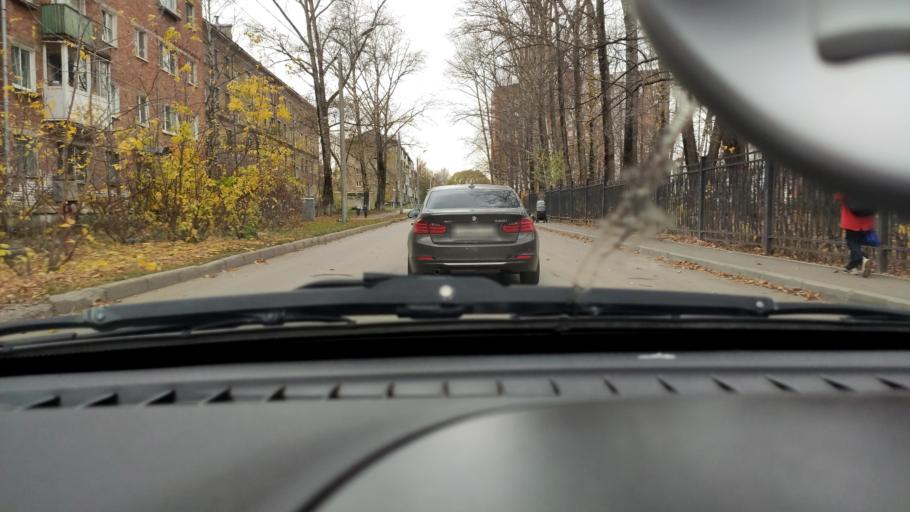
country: RU
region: Perm
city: Perm
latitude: 57.9809
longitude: 56.2030
